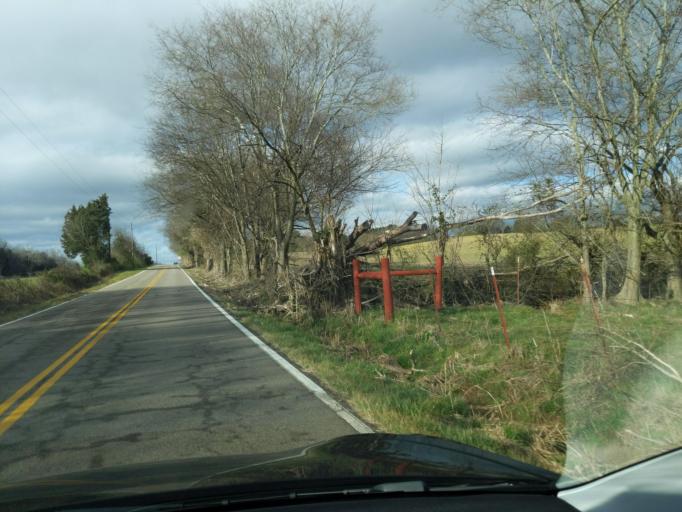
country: US
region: Tennessee
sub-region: Jefferson County
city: Dandridge
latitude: 36.0679
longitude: -83.3897
